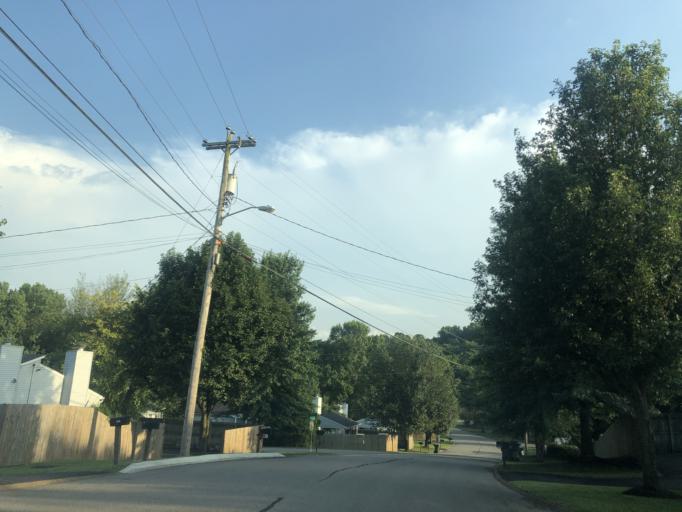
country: US
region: Tennessee
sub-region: Davidson County
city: Lakewood
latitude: 36.1436
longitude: -86.6409
